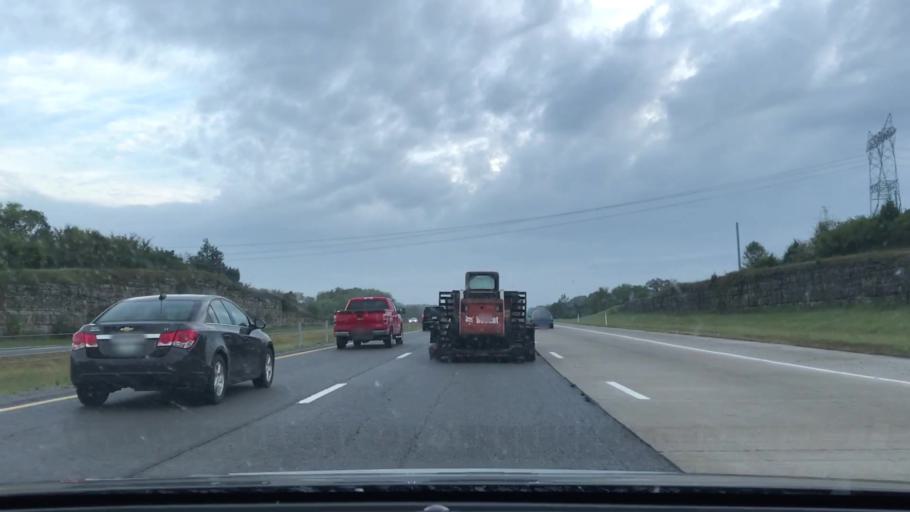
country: US
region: Tennessee
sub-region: Sumner County
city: Gallatin
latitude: 36.3611
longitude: -86.5291
